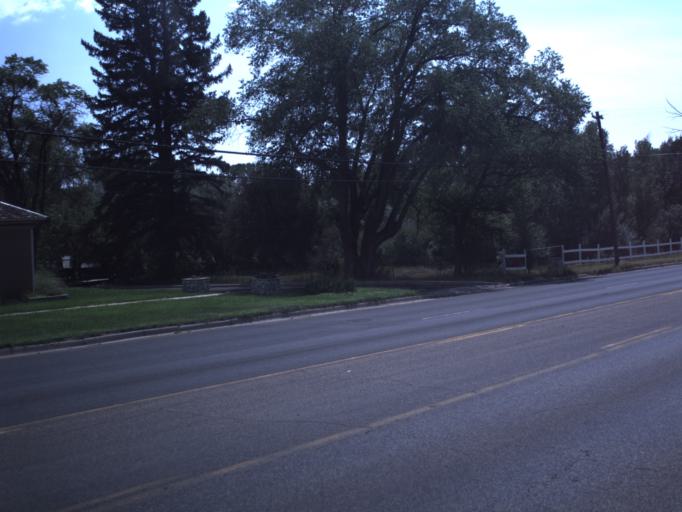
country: US
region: Utah
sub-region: Uintah County
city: Vernal
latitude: 40.4693
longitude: -109.5289
